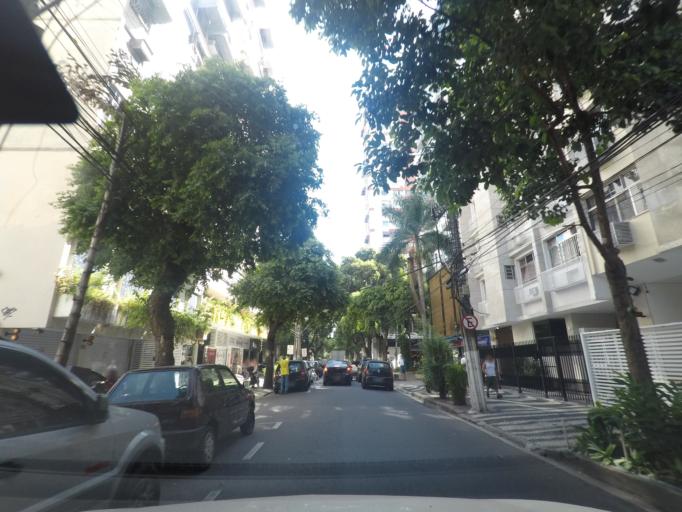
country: BR
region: Rio de Janeiro
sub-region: Niteroi
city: Niteroi
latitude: -22.9033
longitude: -43.1117
